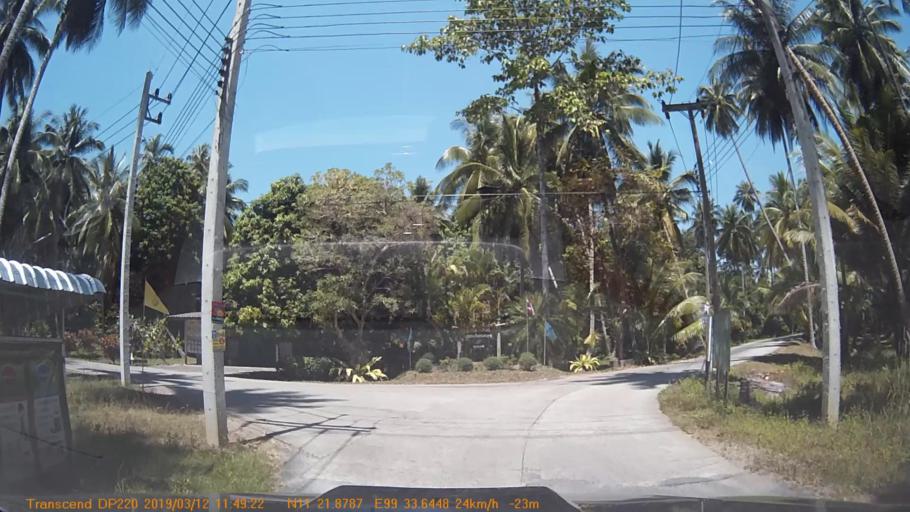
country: TH
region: Prachuap Khiri Khan
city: Thap Sakae
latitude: 11.3648
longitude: 99.5607
